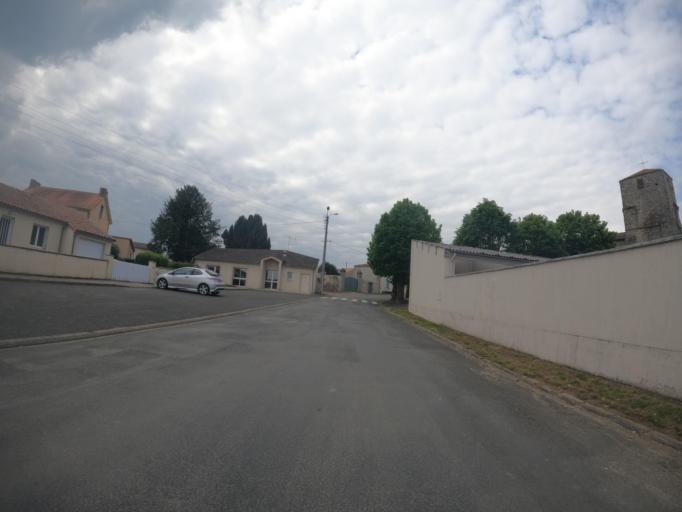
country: FR
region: Poitou-Charentes
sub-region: Departement des Deux-Sevres
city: Saint-Varent
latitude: 46.8683
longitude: -0.3005
